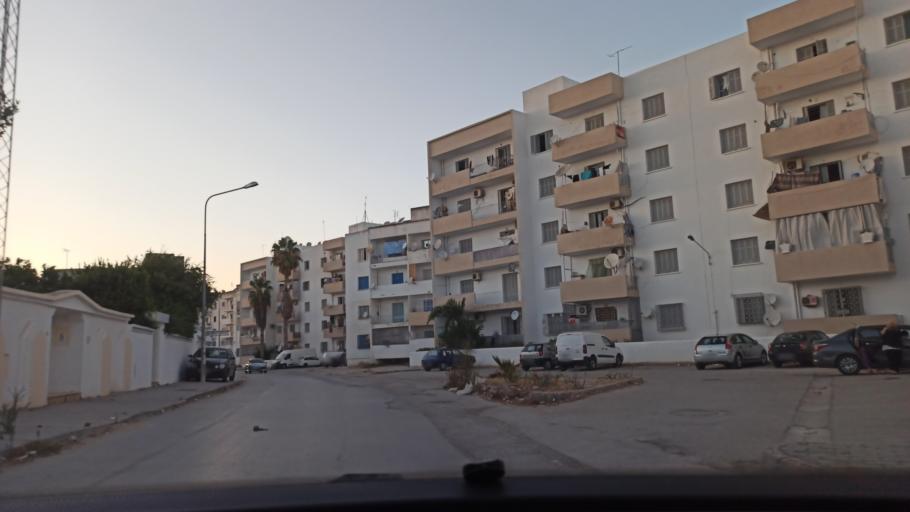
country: TN
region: Ariana
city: Ariana
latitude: 36.8648
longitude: 10.1988
